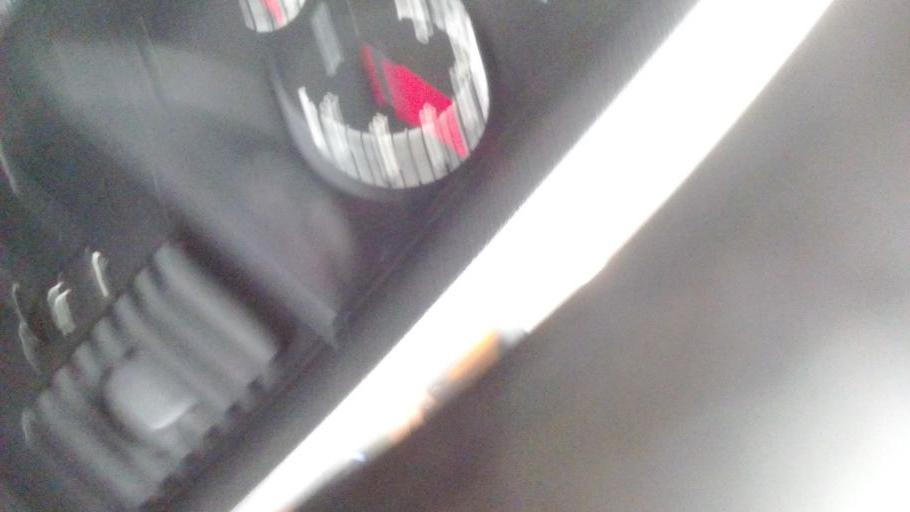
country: IT
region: Molise
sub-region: Provincia di Campobasso
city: Salcito
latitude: 41.7729
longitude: 14.4940
